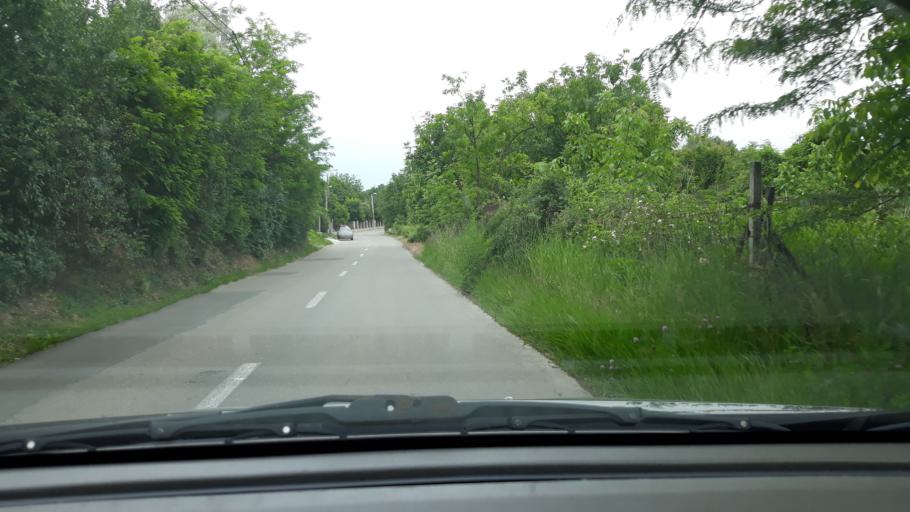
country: RO
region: Bihor
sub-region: Comuna Sanmartin
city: Sanmartin
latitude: 47.0523
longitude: 21.9802
